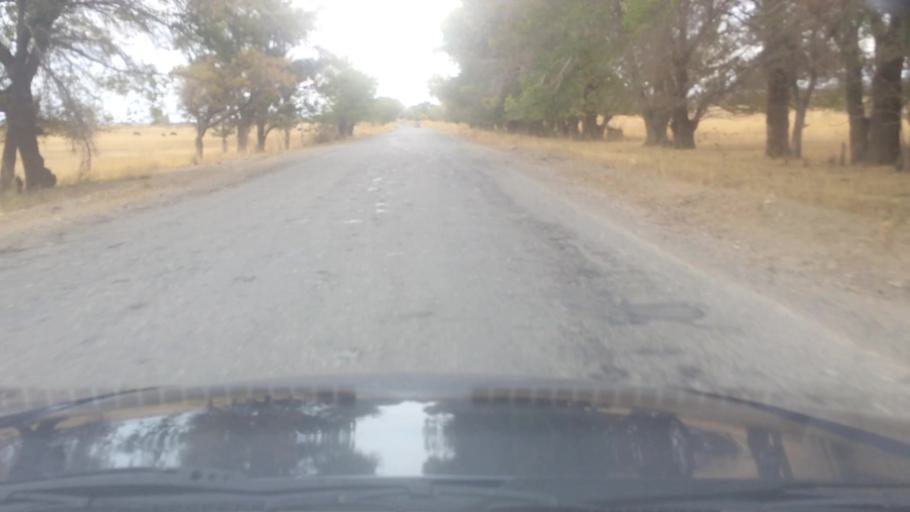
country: KG
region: Ysyk-Koel
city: Balykchy
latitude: 42.3082
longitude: 76.4647
